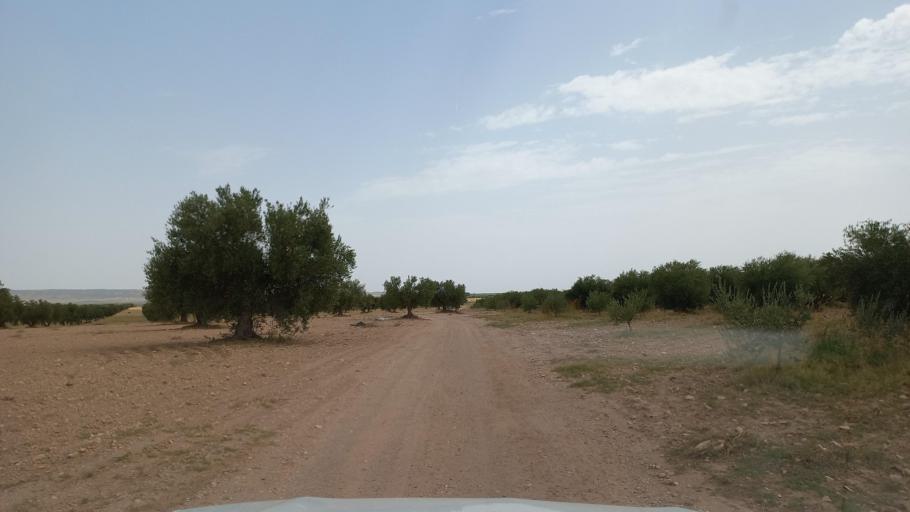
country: TN
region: Al Qasrayn
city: Kasserine
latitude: 35.2899
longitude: 9.0241
